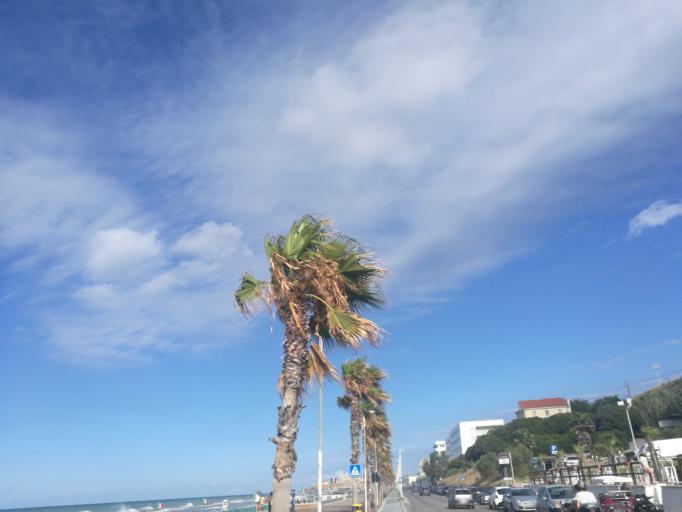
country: IT
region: Molise
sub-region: Provincia di Campobasso
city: Termoli
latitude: 42.0065
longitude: 14.9788
